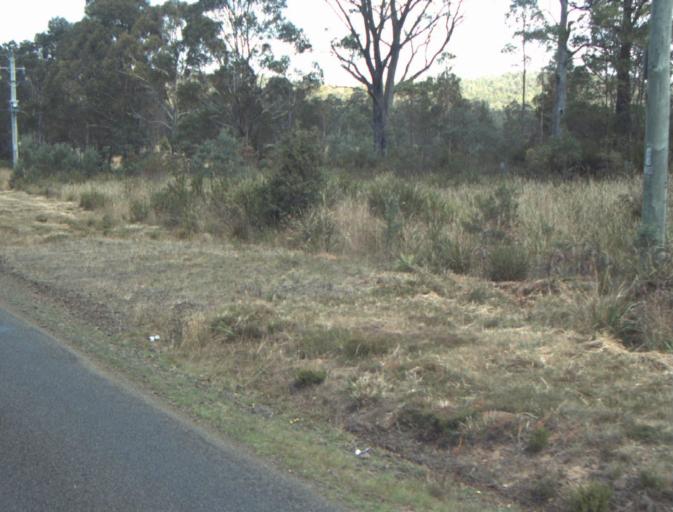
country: AU
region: Tasmania
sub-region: Launceston
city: Mayfield
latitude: -41.3152
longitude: 147.1353
